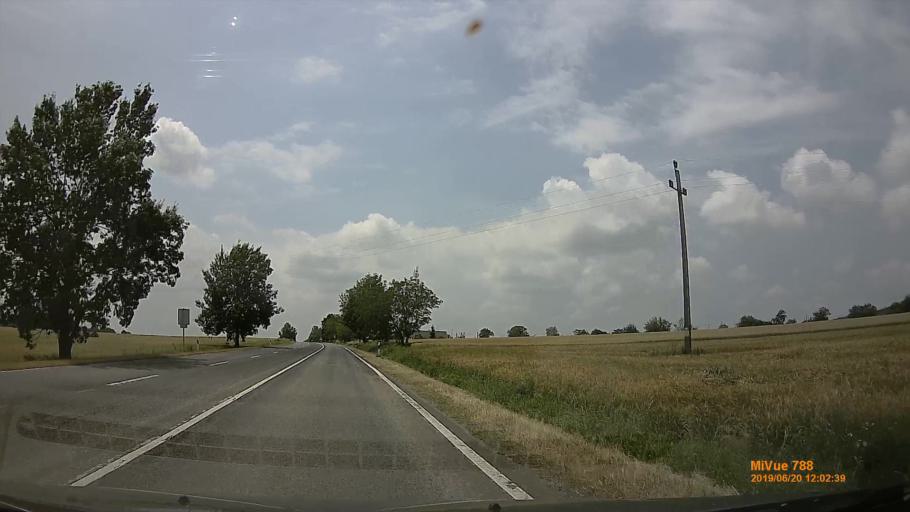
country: HU
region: Baranya
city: Pecsvarad
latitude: 46.1745
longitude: 18.4402
